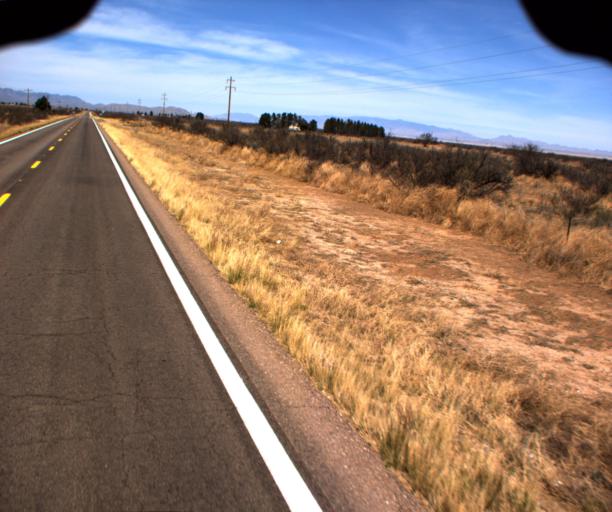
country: US
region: Arizona
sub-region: Cochise County
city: Willcox
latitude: 32.0905
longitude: -109.9063
